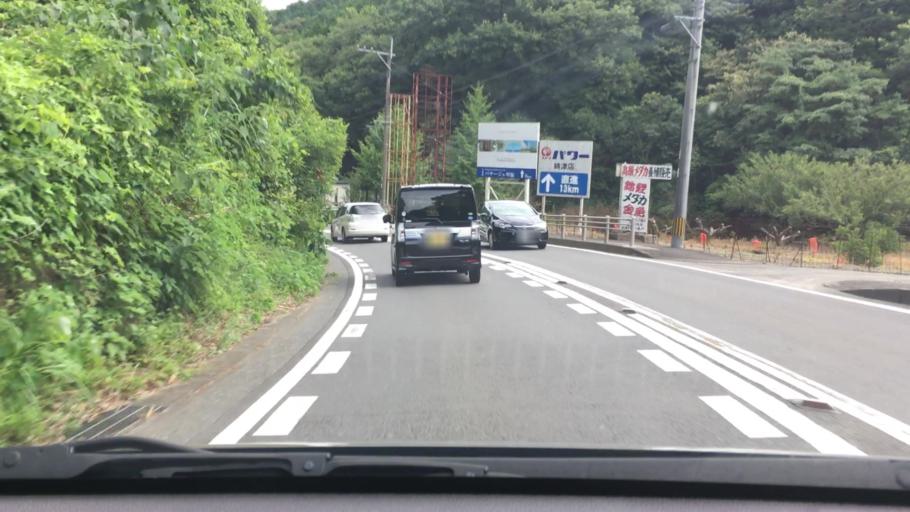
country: JP
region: Nagasaki
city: Togitsu
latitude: 32.9293
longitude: 129.7826
